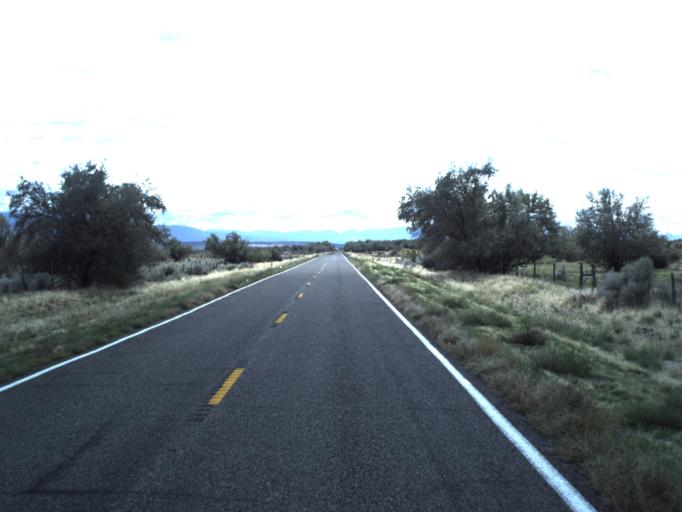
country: US
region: Utah
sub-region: Millard County
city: Fillmore
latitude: 39.0978
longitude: -112.4101
